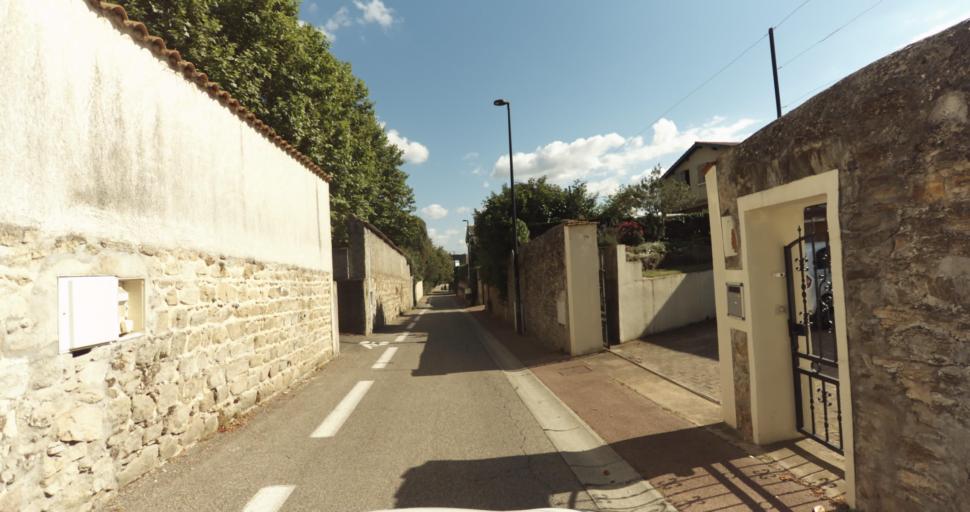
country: FR
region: Rhone-Alpes
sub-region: Departement du Rhone
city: Chaponost
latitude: 45.7143
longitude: 4.7445
